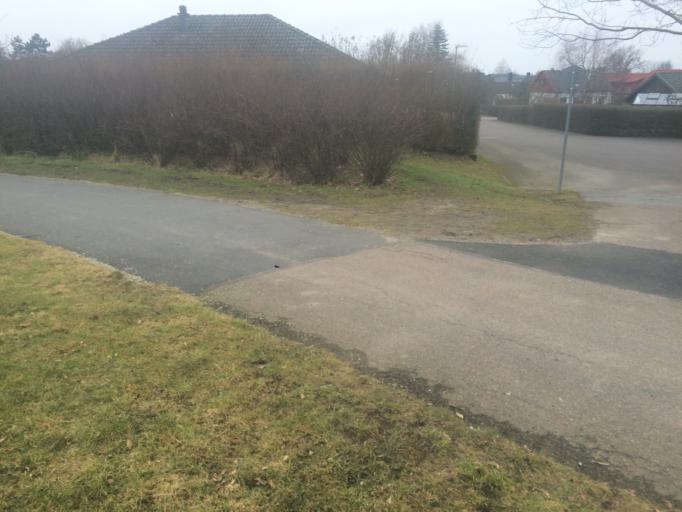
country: SE
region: Skane
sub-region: Kavlinge Kommun
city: Kaevlinge
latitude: 55.7785
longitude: 13.1109
